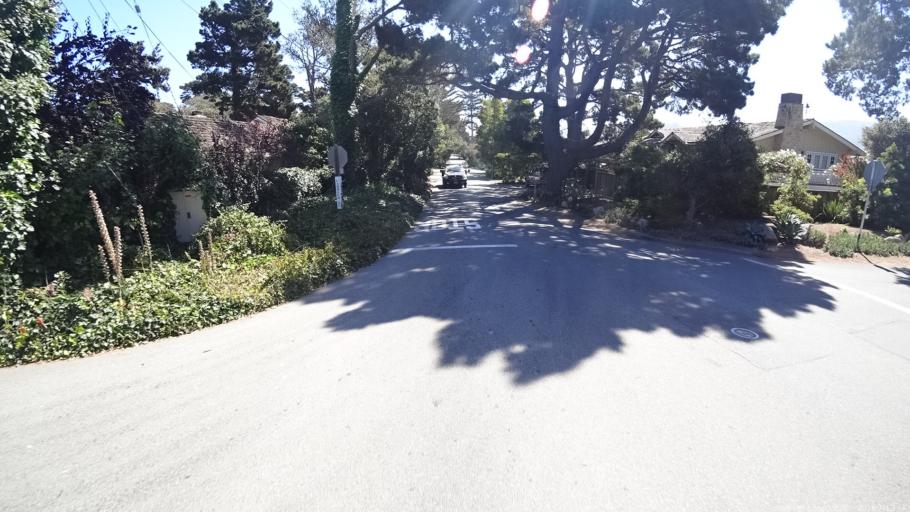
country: US
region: California
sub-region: Monterey County
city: Carmel-by-the-Sea
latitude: 36.5452
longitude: -121.9269
